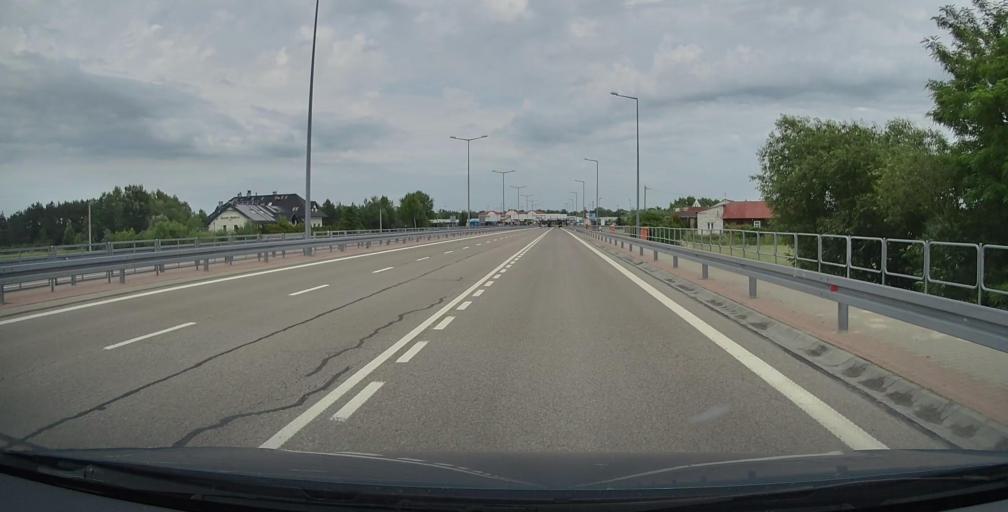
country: PL
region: Lublin Voivodeship
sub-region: Powiat bialski
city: Terespol
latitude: 52.0676
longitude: 23.6377
